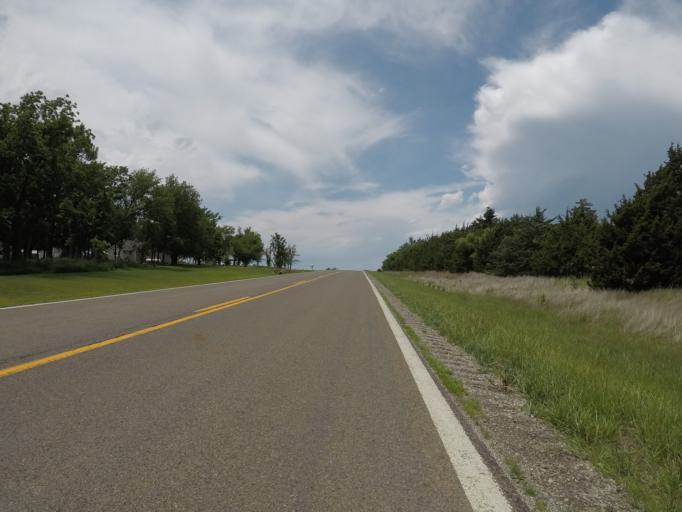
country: US
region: Kansas
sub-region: Wabaunsee County
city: Alma
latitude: 38.8551
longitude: -96.3948
